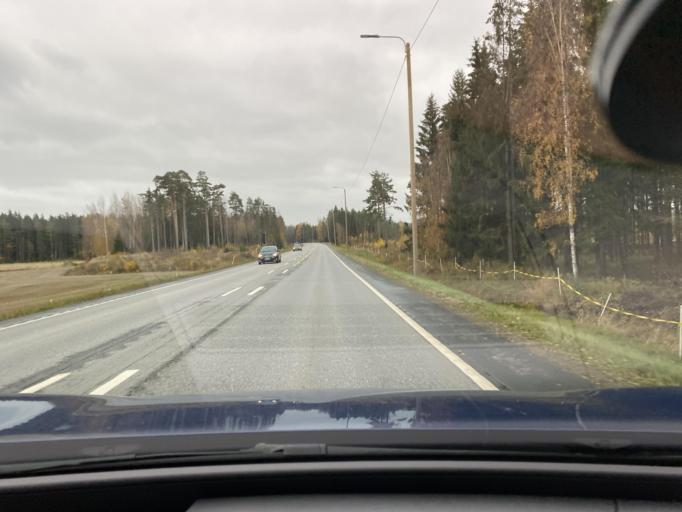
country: FI
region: Varsinais-Suomi
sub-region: Vakka-Suomi
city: Laitila
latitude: 60.9396
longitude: 21.6027
